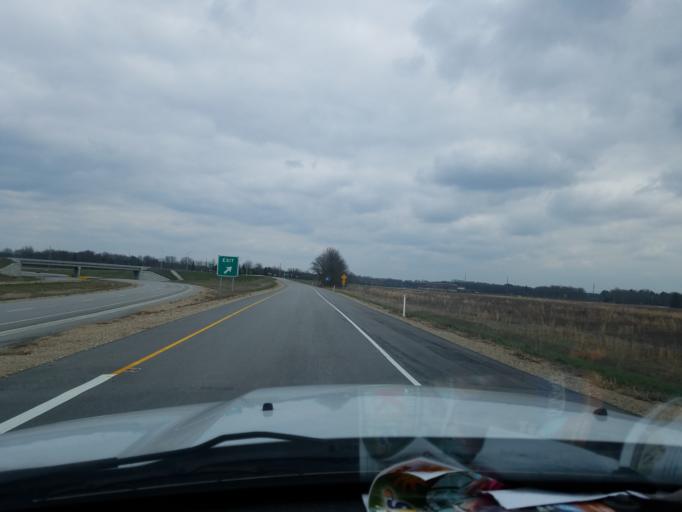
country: US
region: Indiana
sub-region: Vigo County
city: Terre Haute
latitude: 39.4120
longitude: -87.3387
